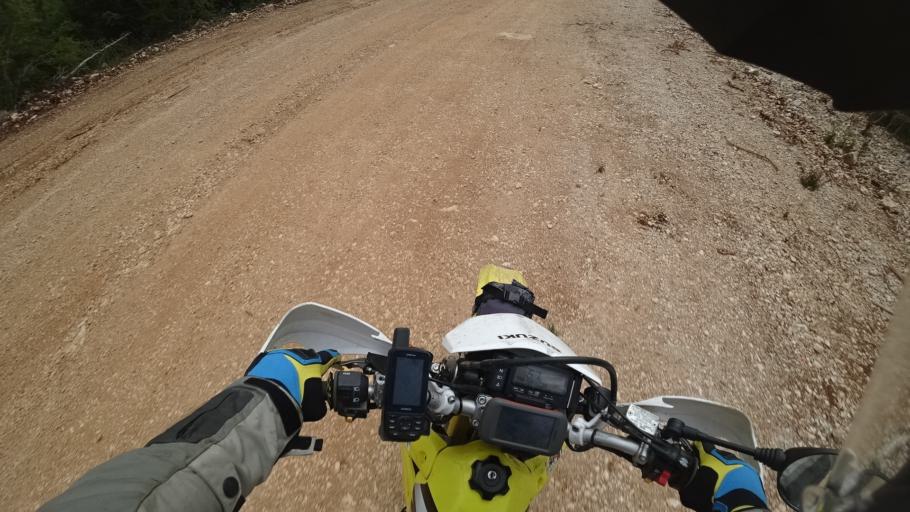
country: HR
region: Sibensko-Kniniska
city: Knin
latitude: 44.0896
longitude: 16.0707
